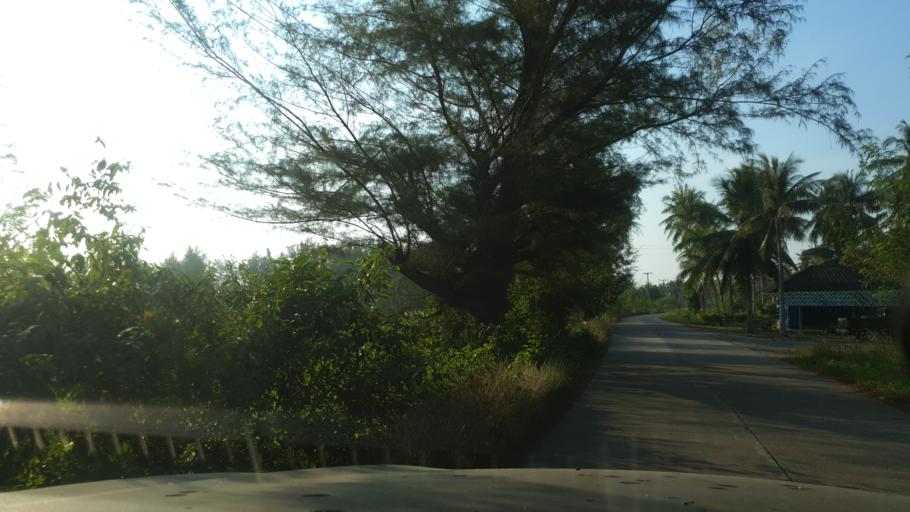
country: TH
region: Prachuap Khiri Khan
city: Bang Saphan
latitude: 11.2846
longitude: 99.5490
